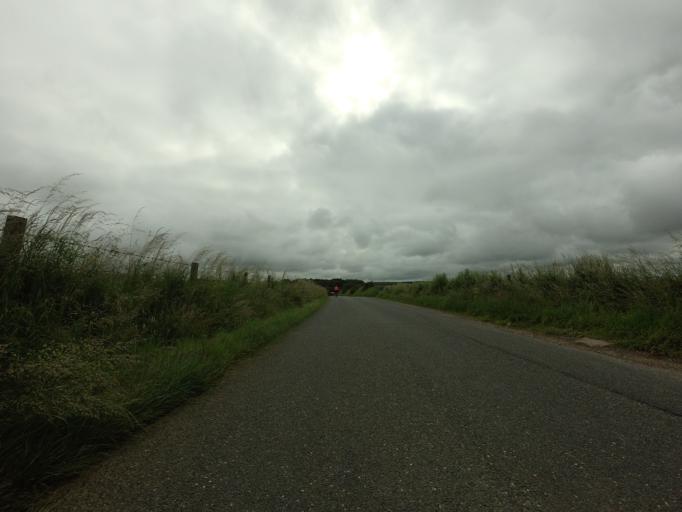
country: GB
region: Scotland
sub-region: Aberdeenshire
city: Turriff
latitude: 57.5339
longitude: -2.4229
